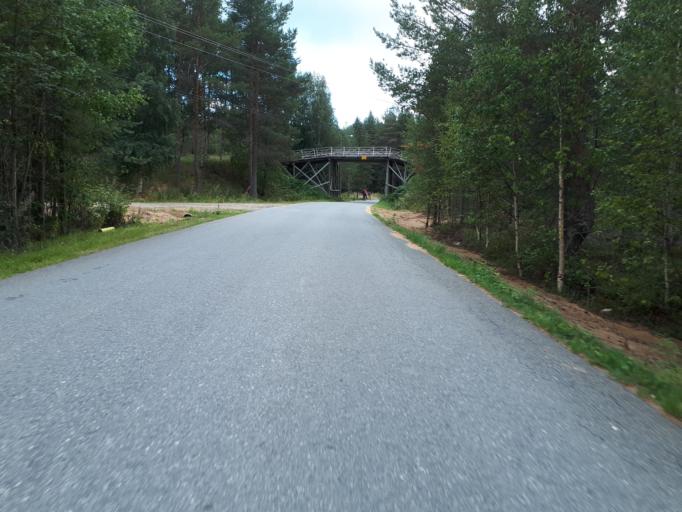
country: FI
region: Northern Ostrobothnia
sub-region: Oulunkaari
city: Ii
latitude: 65.3284
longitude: 25.3936
